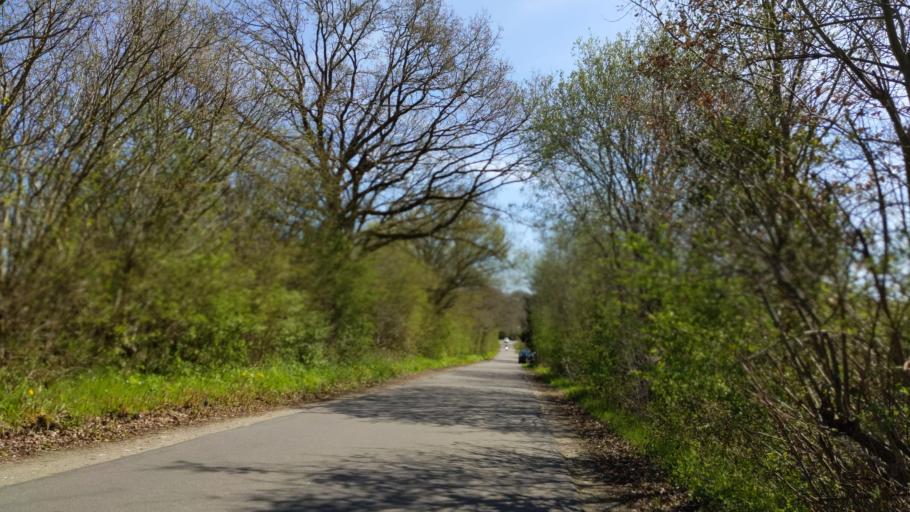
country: DE
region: Schleswig-Holstein
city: Ratekau
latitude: 53.9273
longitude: 10.7674
